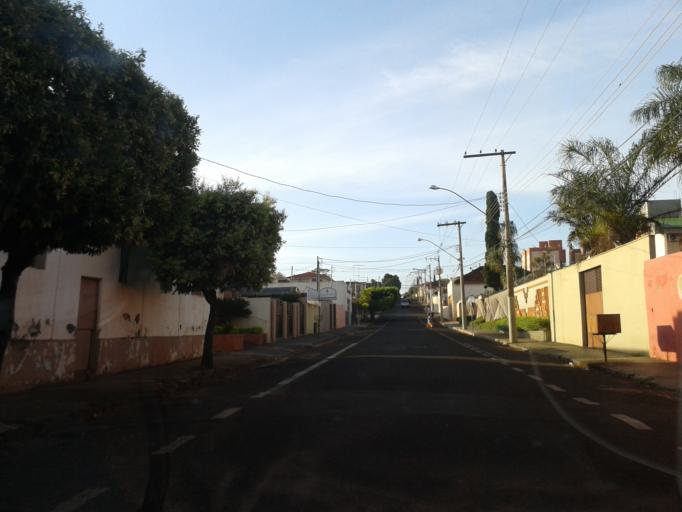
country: BR
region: Minas Gerais
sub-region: Ituiutaba
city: Ituiutaba
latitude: -18.9767
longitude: -49.4631
